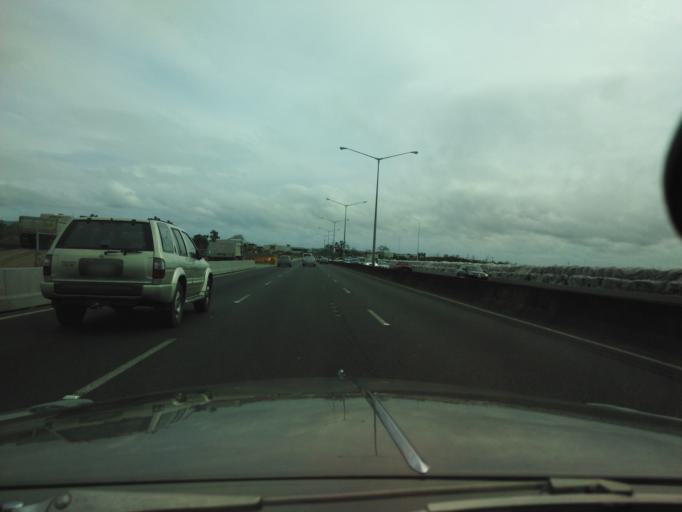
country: NZ
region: Auckland
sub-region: Auckland
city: Rosebank
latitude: -36.8720
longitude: 174.6824
